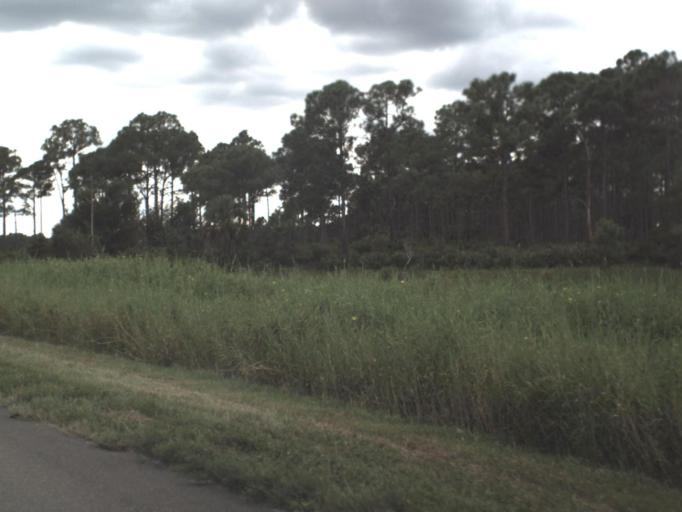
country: US
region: Florida
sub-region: Lee County
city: Olga
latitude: 26.8472
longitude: -81.7598
